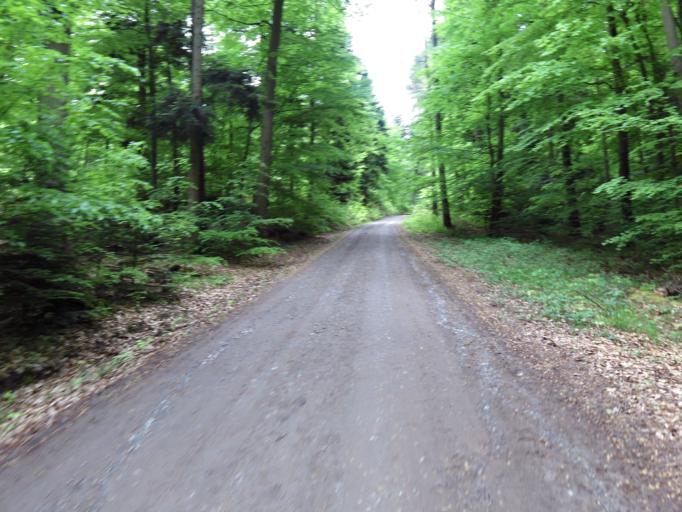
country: DE
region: Rheinland-Pfalz
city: Frankenstein
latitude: 49.4450
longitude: 8.0059
